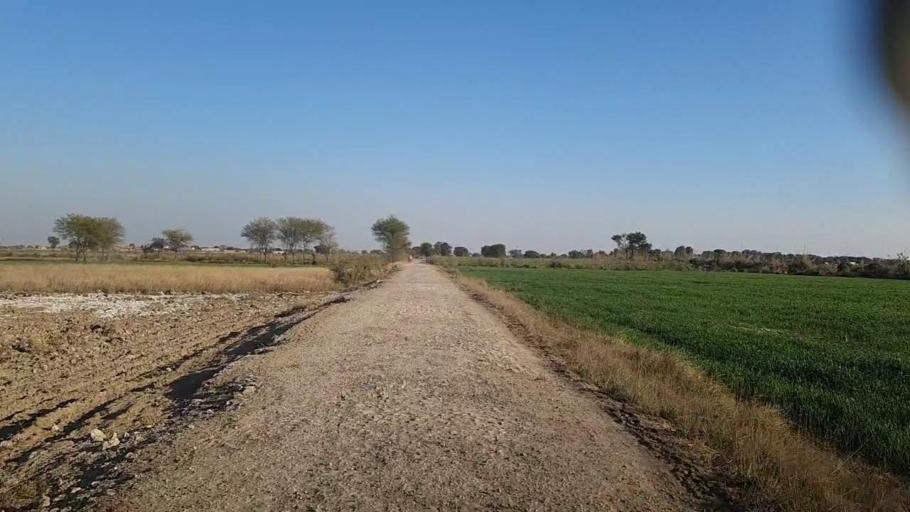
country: PK
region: Sindh
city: Khairpur
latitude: 27.9149
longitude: 69.7289
